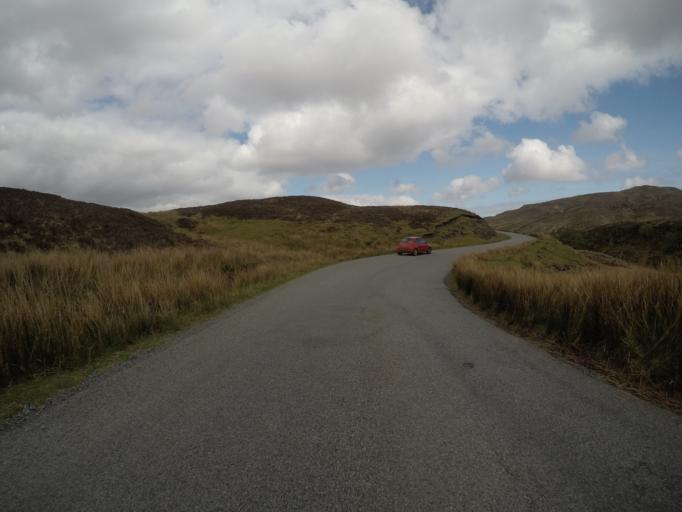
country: GB
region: Scotland
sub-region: Highland
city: Isle of Skye
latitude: 57.3804
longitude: -6.3637
